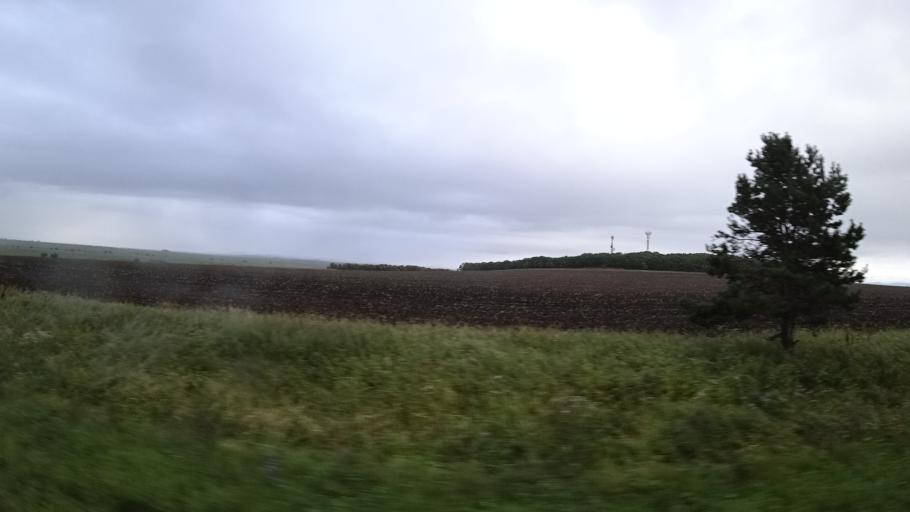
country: RU
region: Primorskiy
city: Chernigovka
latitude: 44.3697
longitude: 132.5317
